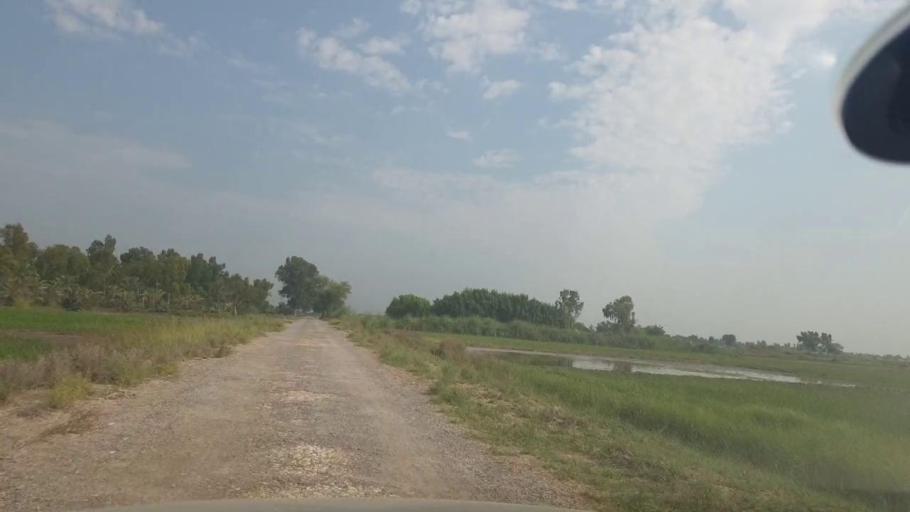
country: PK
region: Balochistan
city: Mehrabpur
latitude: 28.0516
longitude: 68.1231
